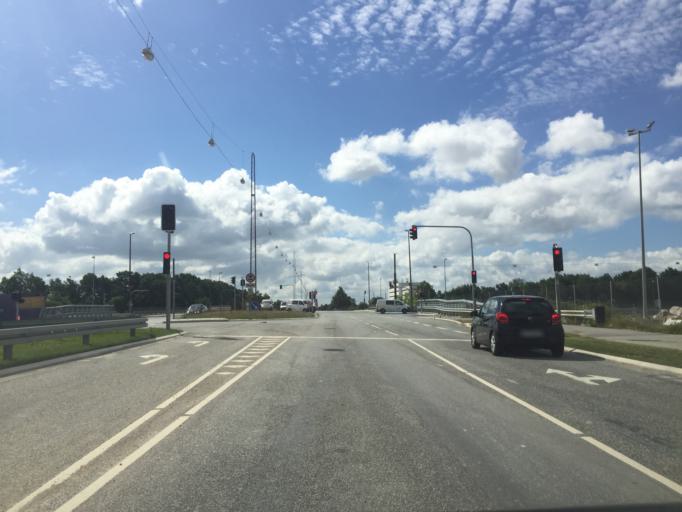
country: DK
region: Capital Region
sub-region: Hvidovre Kommune
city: Hvidovre
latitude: 55.6500
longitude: 12.4581
